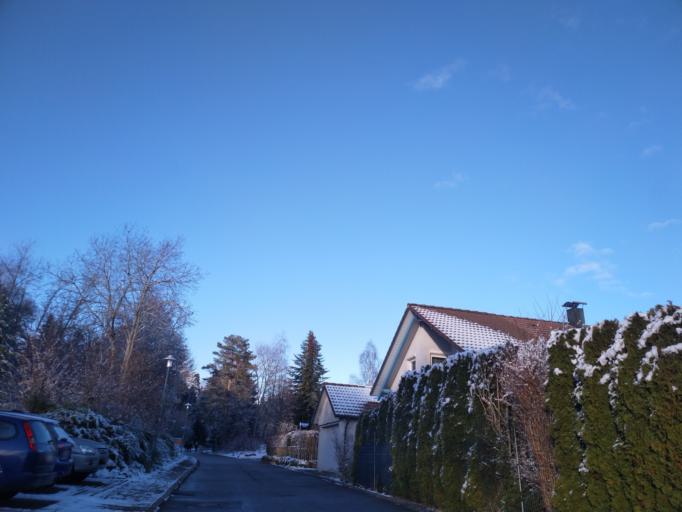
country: DE
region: Baden-Wuerttemberg
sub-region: Karlsruhe Region
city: Simmersfeld
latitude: 48.6239
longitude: 8.5068
